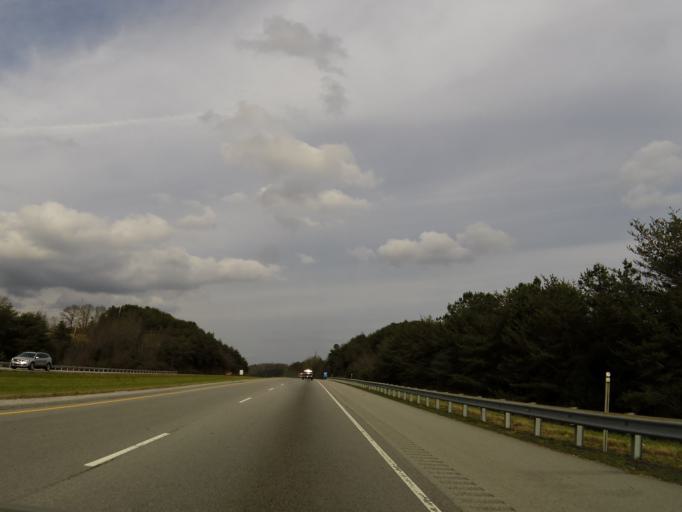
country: US
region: Tennessee
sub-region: Hamilton County
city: Soddy-Daisy
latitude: 35.2656
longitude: -85.1625
